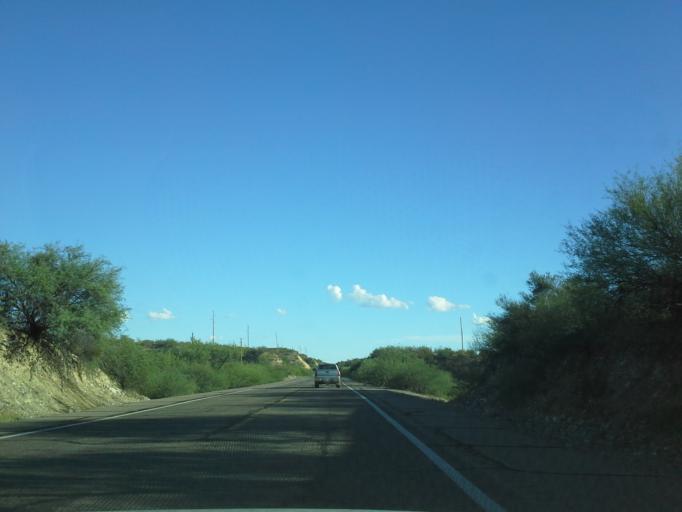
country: US
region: Arizona
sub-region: Pinal County
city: Mammoth
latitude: 32.7833
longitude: -110.6677
